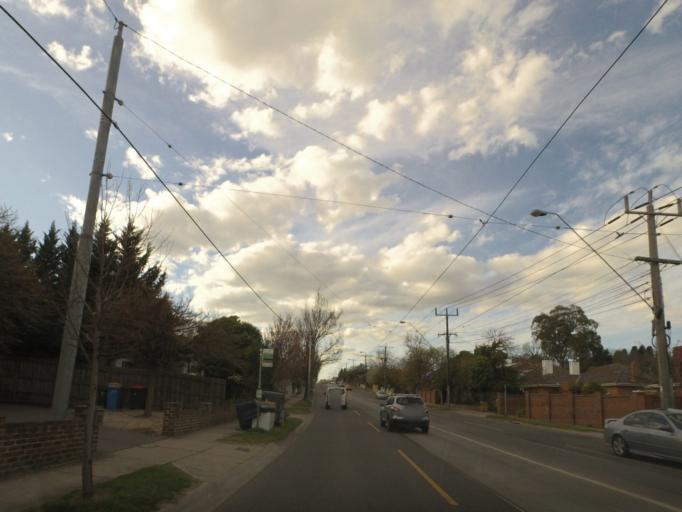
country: AU
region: Victoria
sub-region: Stonnington
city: Glen Iris
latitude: -37.8499
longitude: 145.0530
